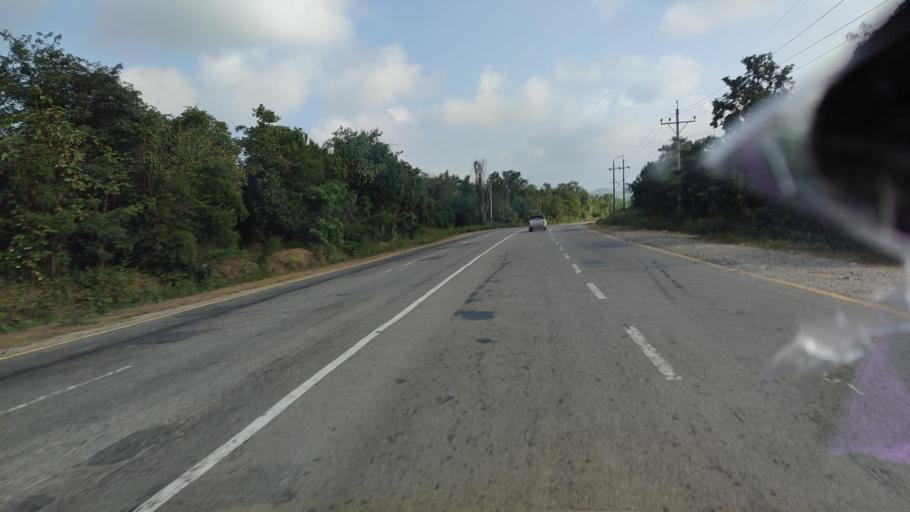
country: MM
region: Mandalay
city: Yamethin
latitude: 20.7757
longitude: 96.3307
